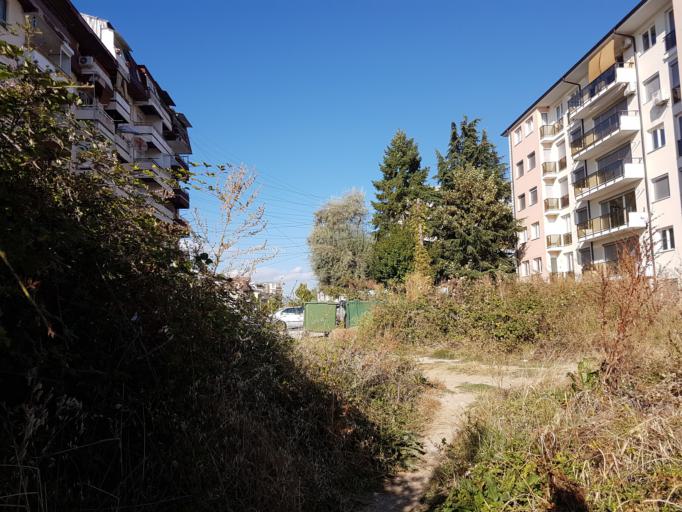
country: MK
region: Ohrid
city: Ohrid
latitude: 41.1220
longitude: 20.7792
